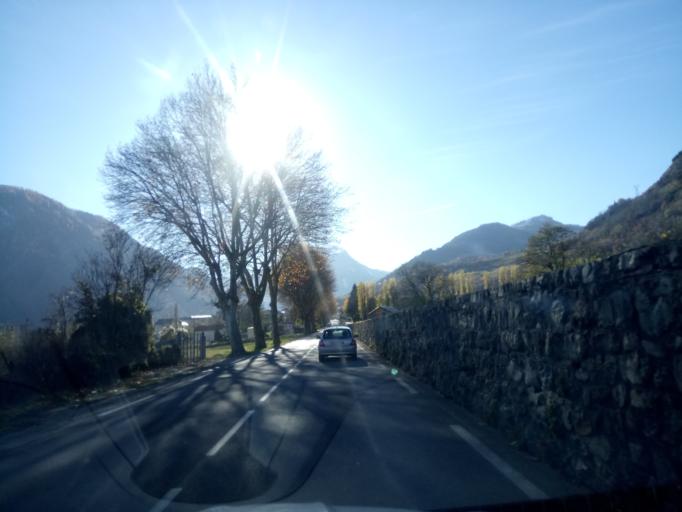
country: FR
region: Rhone-Alpes
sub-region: Departement de la Savoie
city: Saint-Jean-de-Maurienne
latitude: 45.2847
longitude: 6.3506
